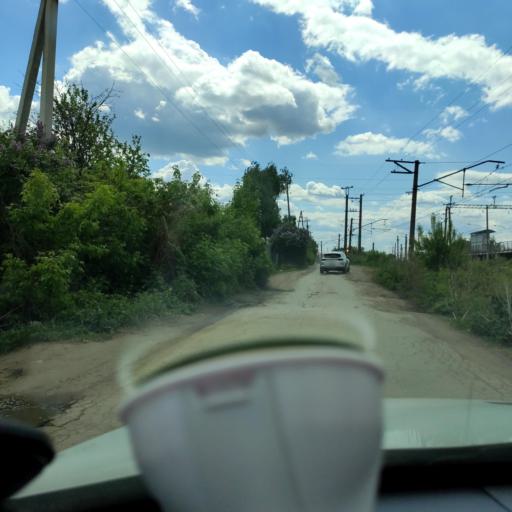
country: RU
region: Samara
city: Petra-Dubrava
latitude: 53.2710
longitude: 50.3178
